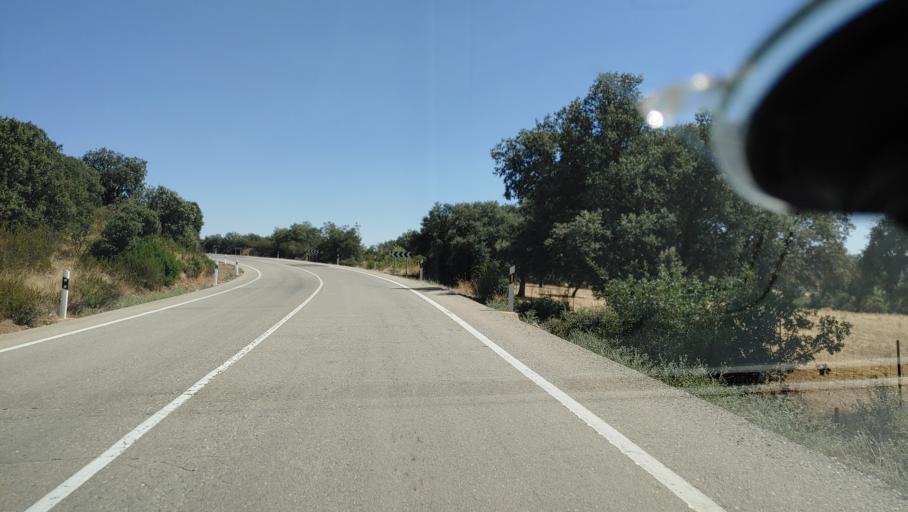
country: ES
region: Castille-La Mancha
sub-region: Provincia de Ciudad Real
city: Saceruela
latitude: 39.0162
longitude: -4.4846
